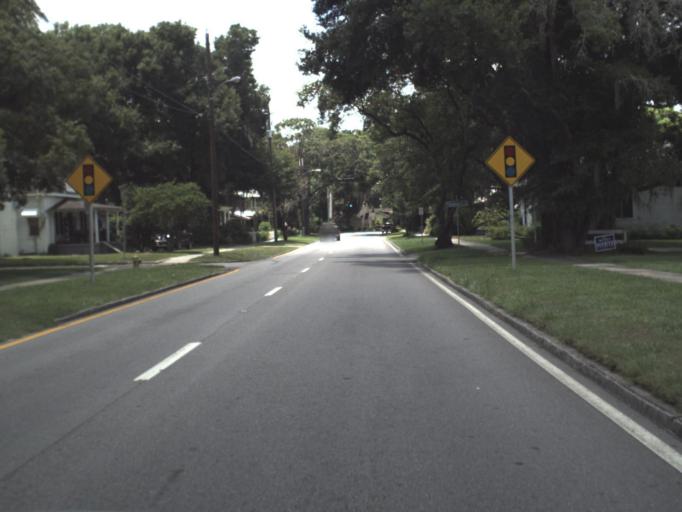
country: US
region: Florida
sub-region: Hillsborough County
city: Plant City
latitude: 28.0172
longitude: -82.1274
